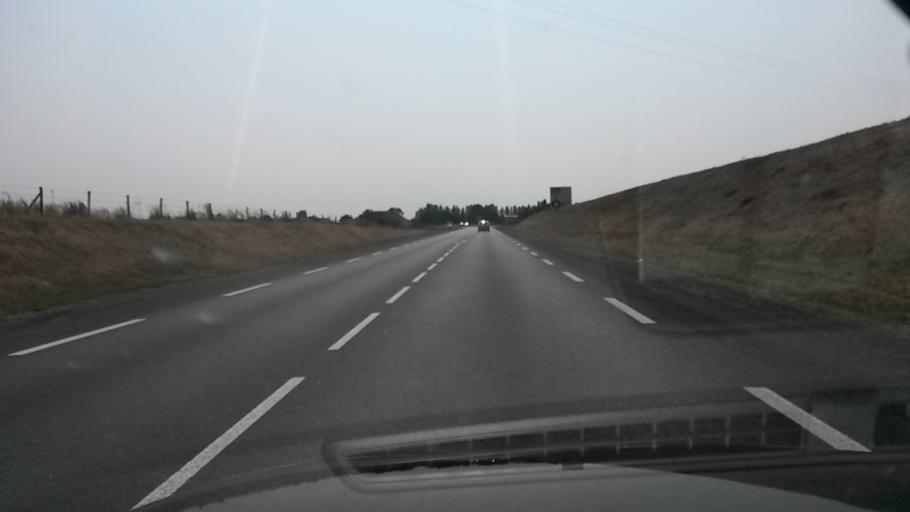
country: FR
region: Pays de la Loire
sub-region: Departement de la Loire-Atlantique
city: Mesanger
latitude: 47.4172
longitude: -1.1864
